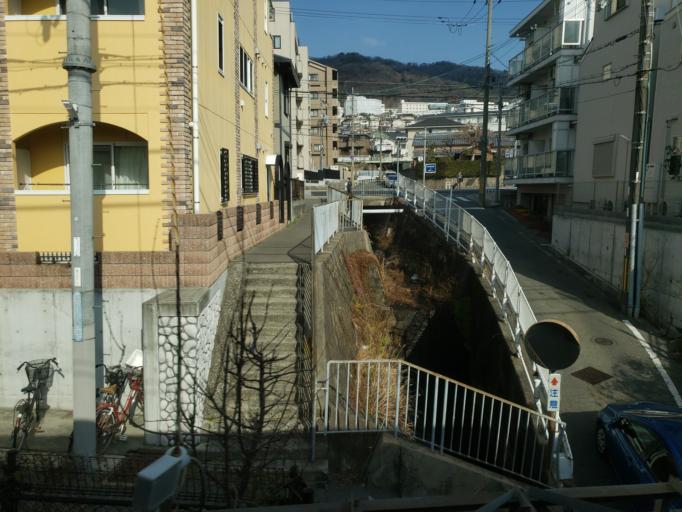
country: JP
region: Hyogo
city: Ashiya
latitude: 34.7298
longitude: 135.2888
